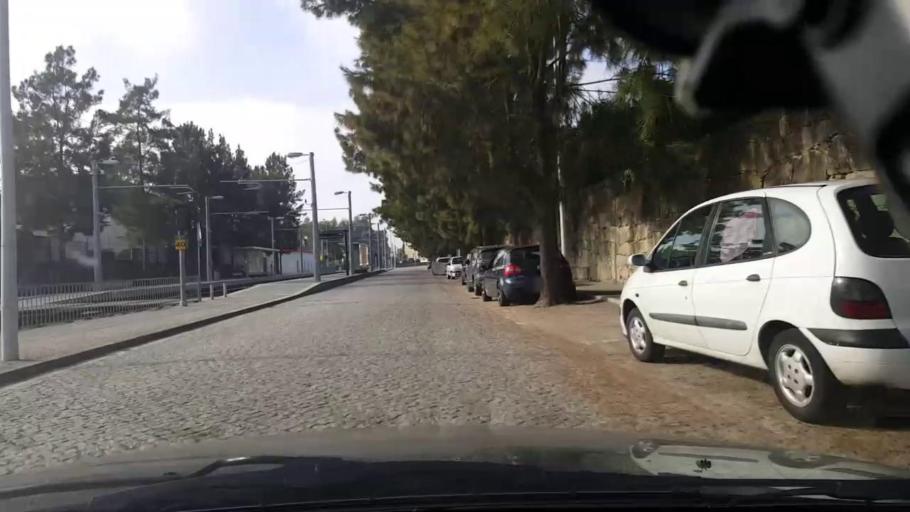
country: PT
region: Porto
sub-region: Maia
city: Gemunde
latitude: 41.2698
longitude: -8.6789
